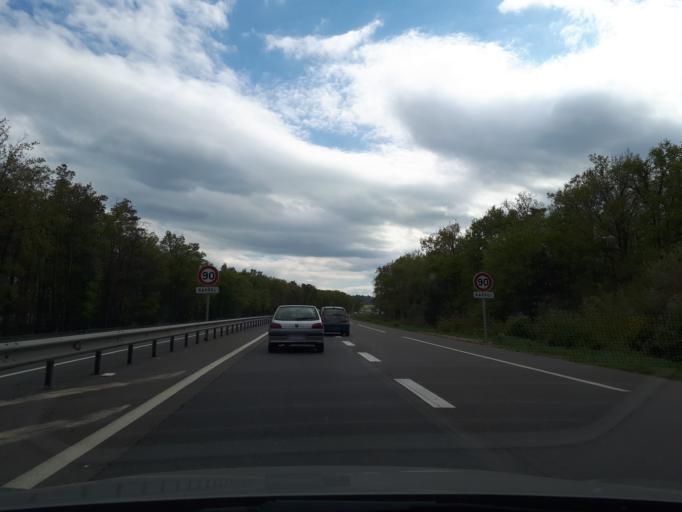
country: FR
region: Rhone-Alpes
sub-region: Departement de la Loire
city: Saint-Bonnet-les-Oules
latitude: 45.5336
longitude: 4.3049
